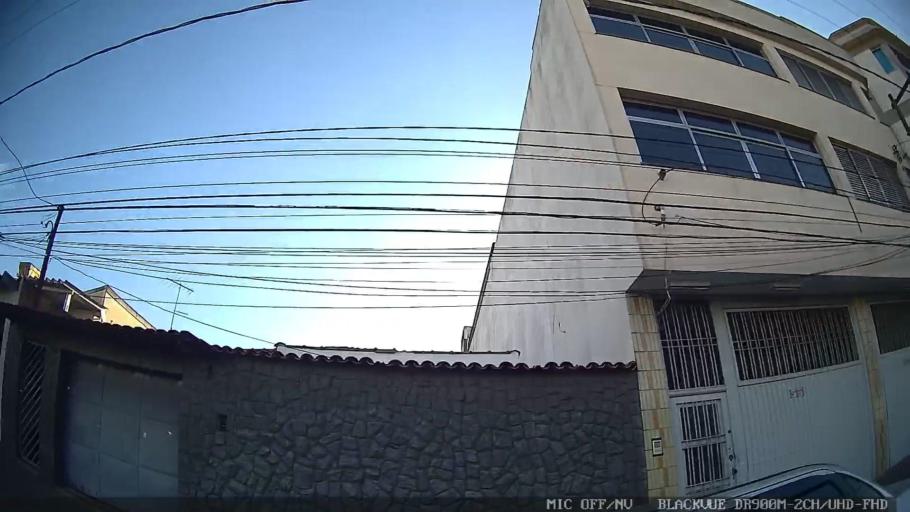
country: BR
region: Sao Paulo
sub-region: Guarulhos
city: Guarulhos
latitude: -23.5338
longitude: -46.5003
